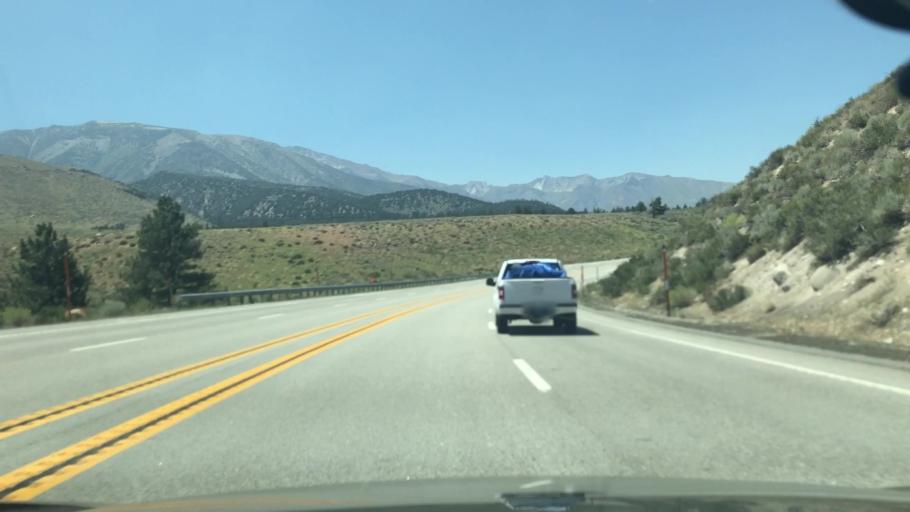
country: US
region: California
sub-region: Inyo County
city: West Bishop
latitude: 37.5593
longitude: -118.6572
